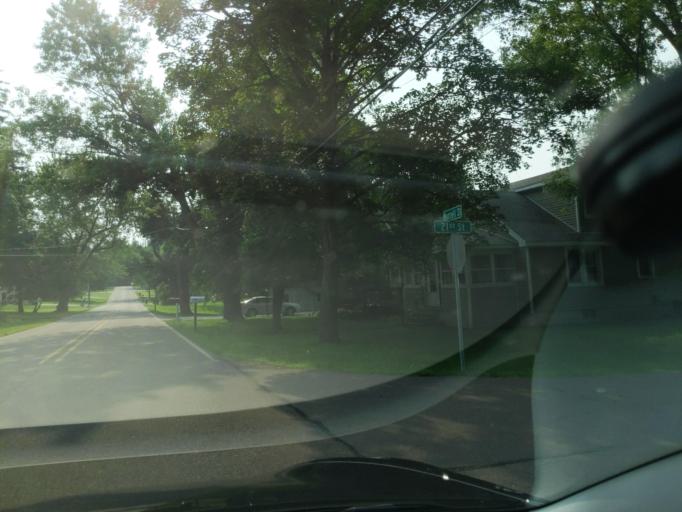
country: US
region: Michigan
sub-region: Jackson County
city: Jackson
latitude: 42.2400
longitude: -84.4392
